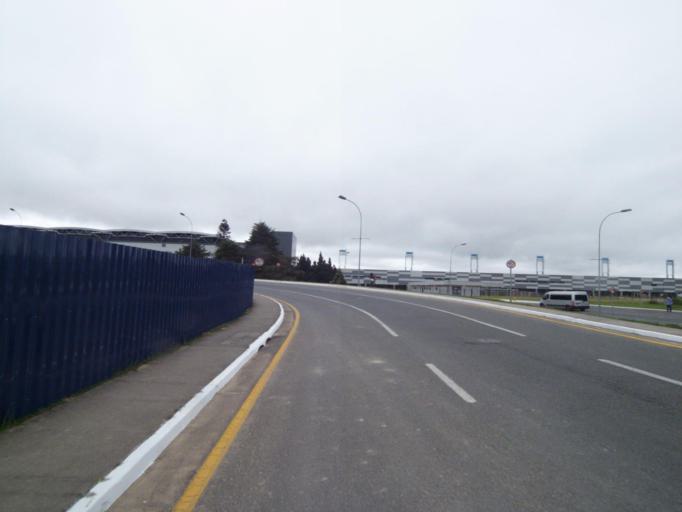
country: BR
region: Parana
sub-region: Sao Jose Dos Pinhais
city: Sao Jose dos Pinhais
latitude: -25.5382
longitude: -49.1732
